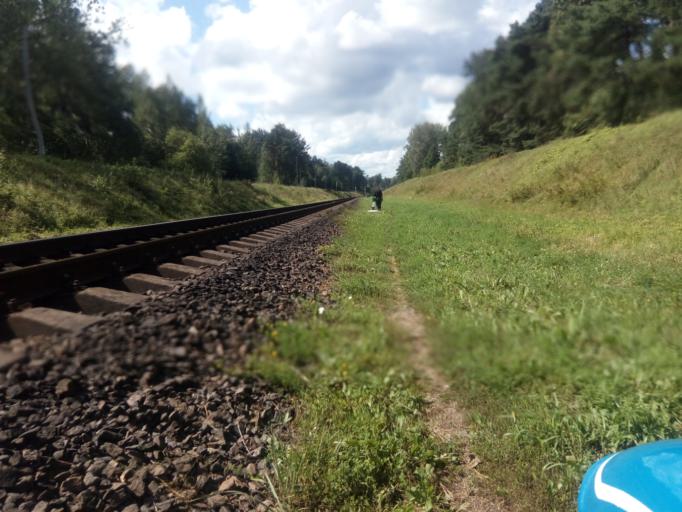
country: BY
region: Vitebsk
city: Dzisna
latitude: 55.6782
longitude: 28.2984
